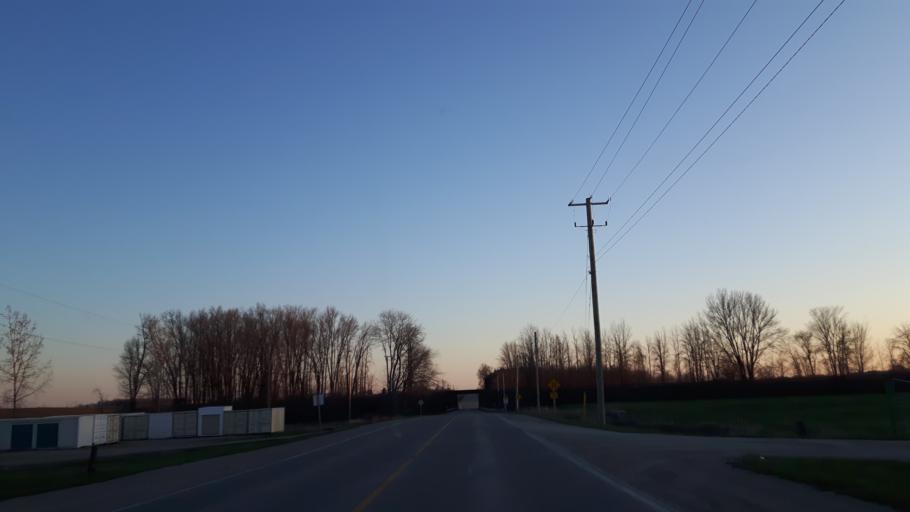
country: CA
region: Ontario
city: Bluewater
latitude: 43.6081
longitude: -81.5445
